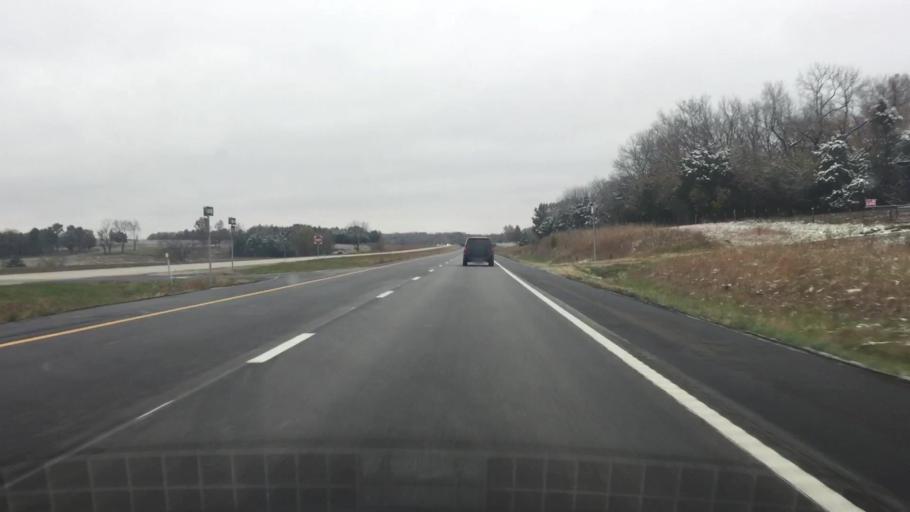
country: US
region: Missouri
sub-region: Saint Clair County
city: Osceola
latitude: 38.0008
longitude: -93.6549
